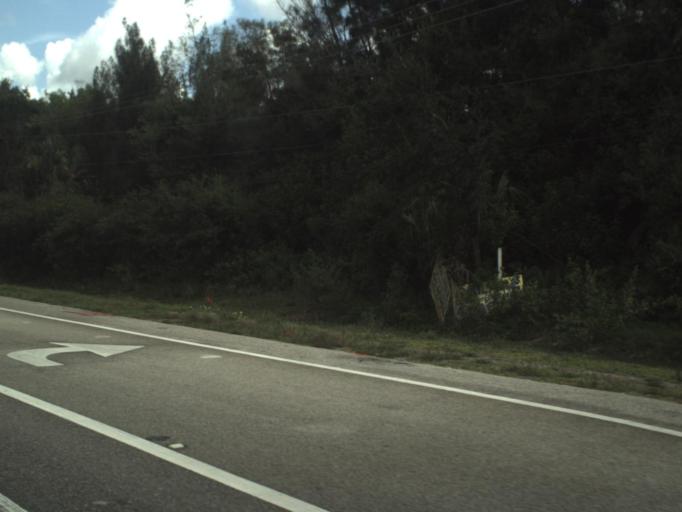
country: US
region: Florida
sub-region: Palm Beach County
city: Palm Beach Gardens
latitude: 26.7873
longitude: -80.1184
